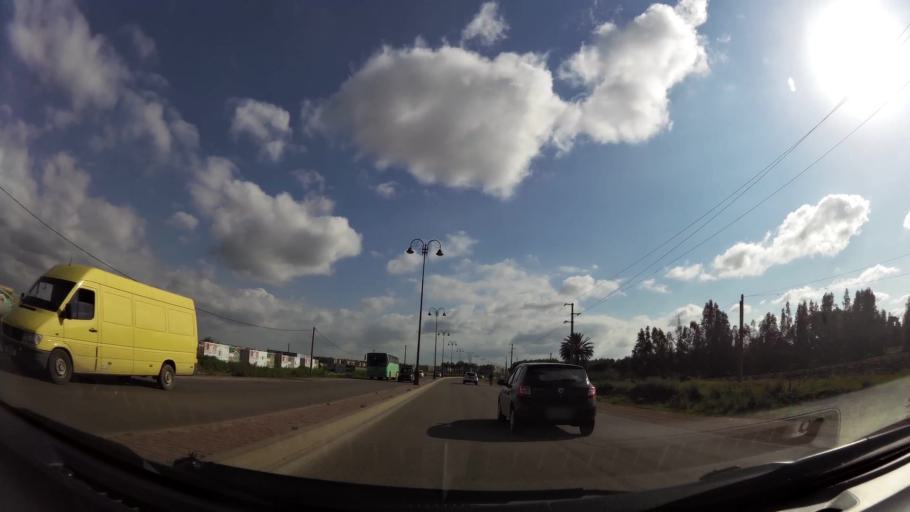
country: MA
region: Chaouia-Ouardigha
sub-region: Settat Province
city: Berrechid
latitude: 33.2858
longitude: -7.5779
